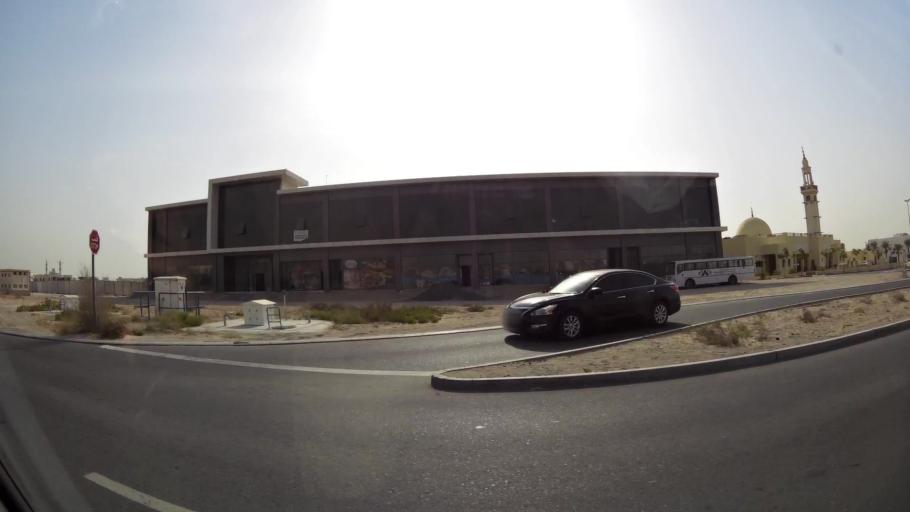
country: AE
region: Ash Shariqah
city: Sharjah
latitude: 25.2442
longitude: 55.4536
